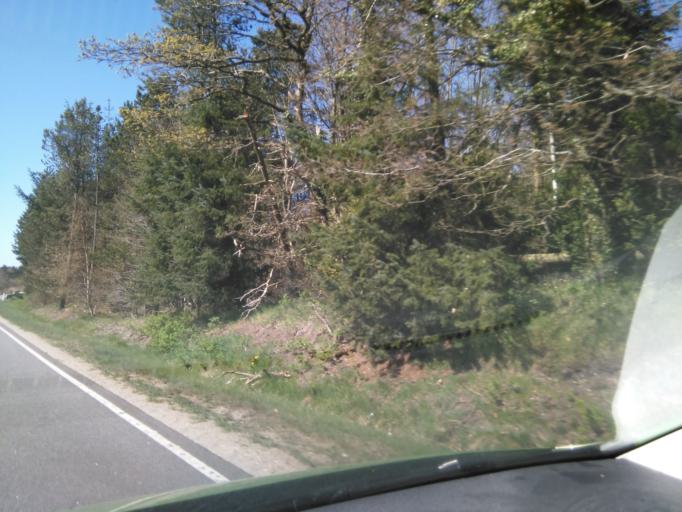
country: DK
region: South Denmark
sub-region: Varde Kommune
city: Varde
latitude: 55.6279
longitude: 8.4157
